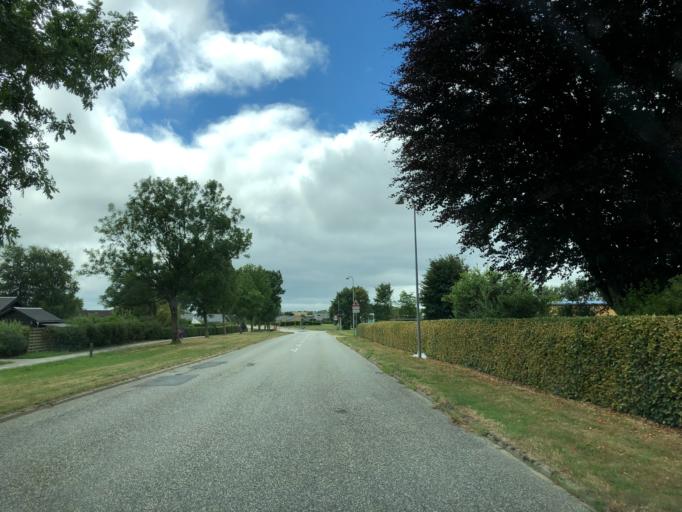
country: DK
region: Central Jutland
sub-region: Herning Kommune
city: Vildbjerg
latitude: 56.1918
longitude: 8.7567
